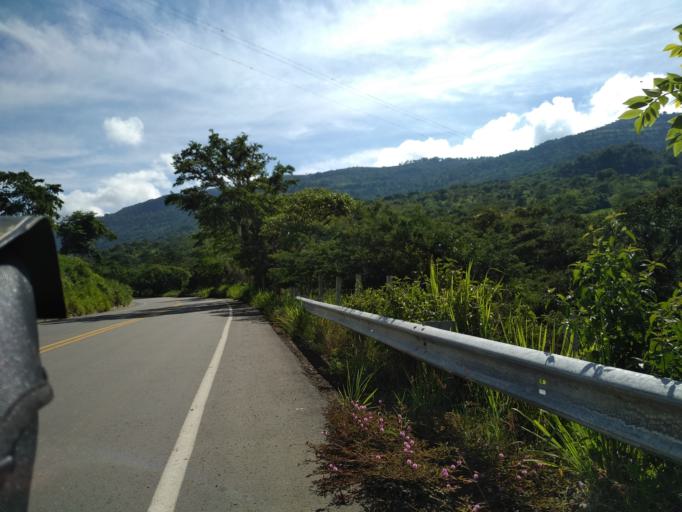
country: CO
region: Santander
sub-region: San Gil
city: San Gil
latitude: 6.5111
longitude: -73.1257
